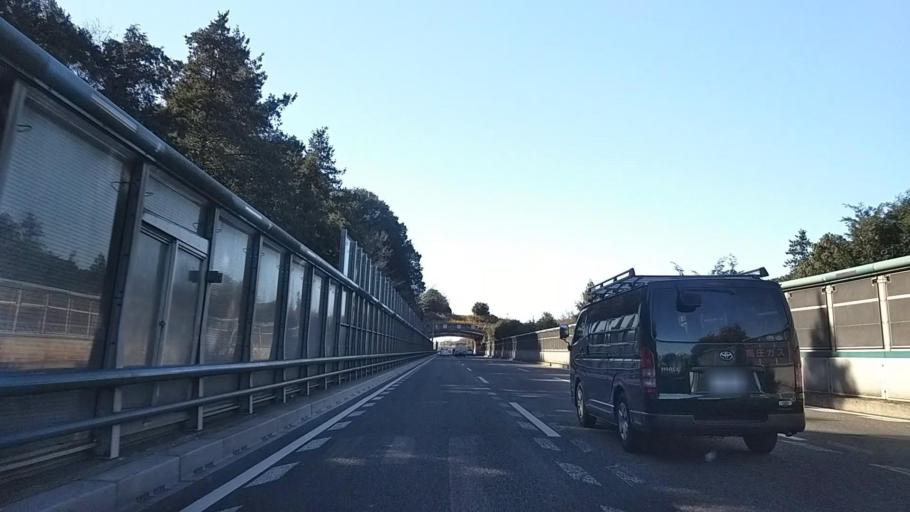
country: JP
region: Kanagawa
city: Yokohama
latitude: 35.4698
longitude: 139.5698
